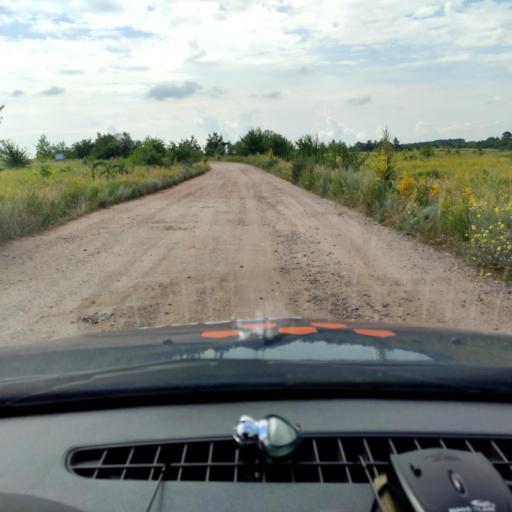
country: RU
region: Voronezj
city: Ramon'
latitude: 52.0720
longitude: 39.3232
